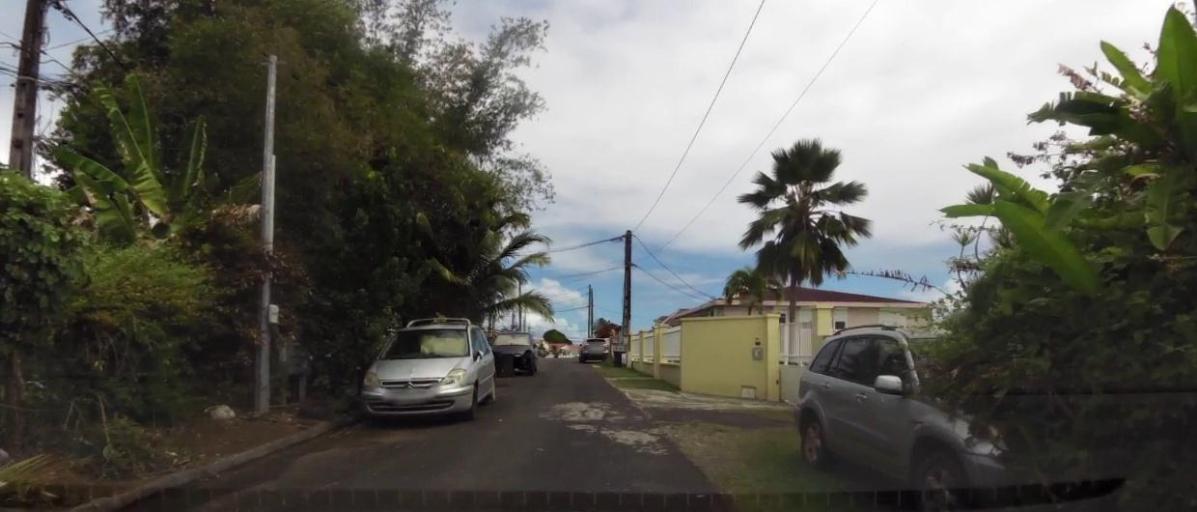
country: GP
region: Guadeloupe
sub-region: Guadeloupe
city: Petit-Bourg
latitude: 16.1974
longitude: -61.5926
